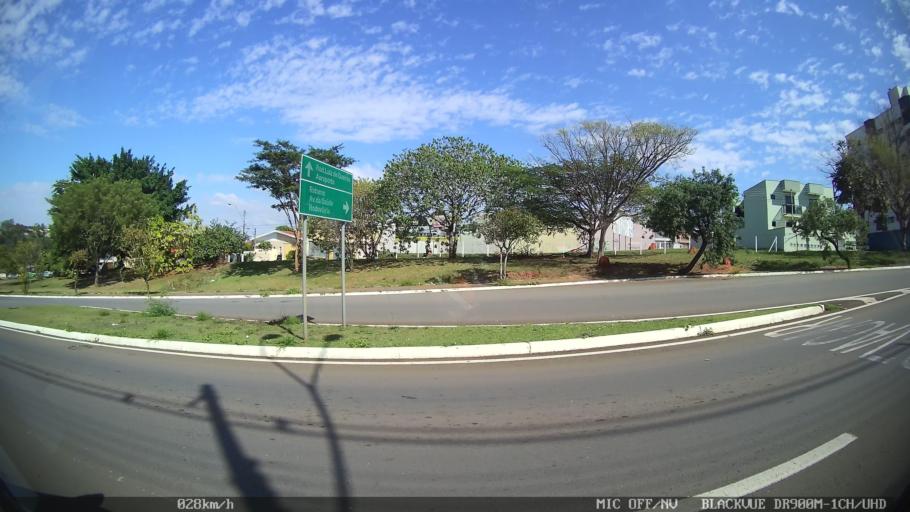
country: BR
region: Sao Paulo
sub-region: Americana
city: Americana
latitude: -22.7432
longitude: -47.3089
